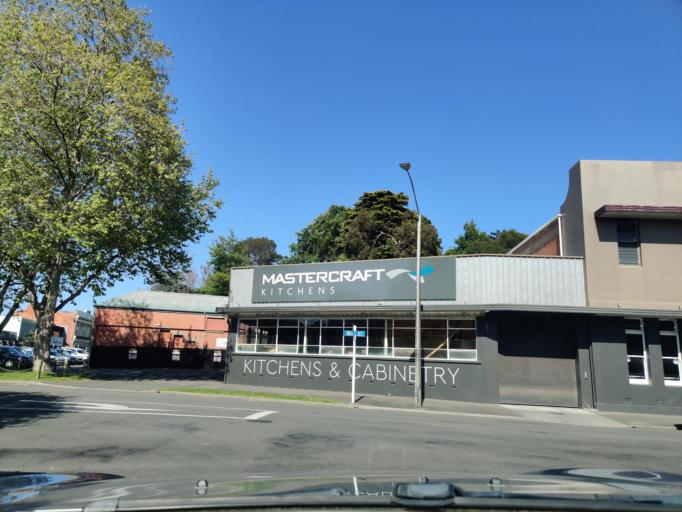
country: NZ
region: Manawatu-Wanganui
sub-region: Wanganui District
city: Wanganui
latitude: -39.9316
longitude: 175.0559
